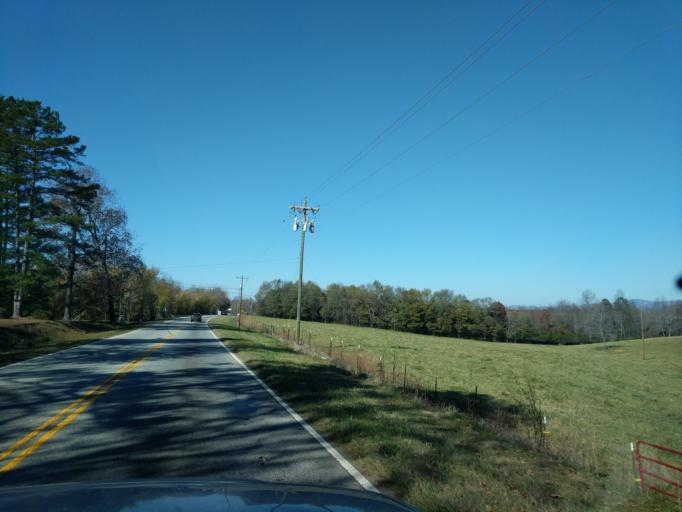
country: US
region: South Carolina
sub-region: Greenville County
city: Taylors
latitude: 34.9719
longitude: -82.3270
